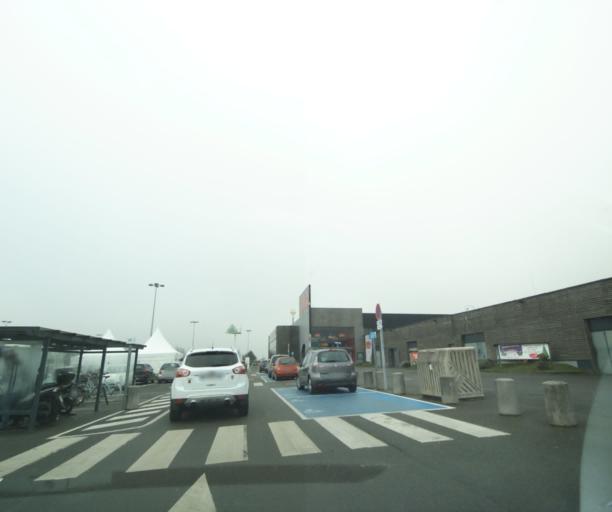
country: FR
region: Ile-de-France
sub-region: Departement de Seine-Saint-Denis
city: Livry-Gargan
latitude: 48.9276
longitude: 2.5534
